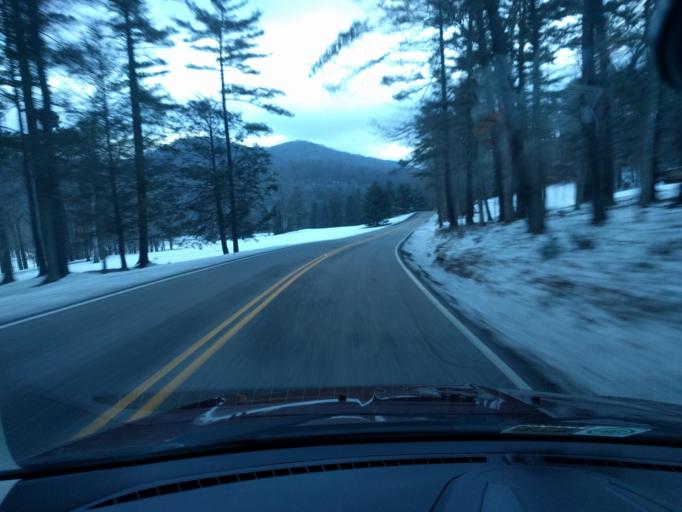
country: US
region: Virginia
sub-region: Bath County
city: Warm Springs
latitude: 37.9526
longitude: -79.8691
